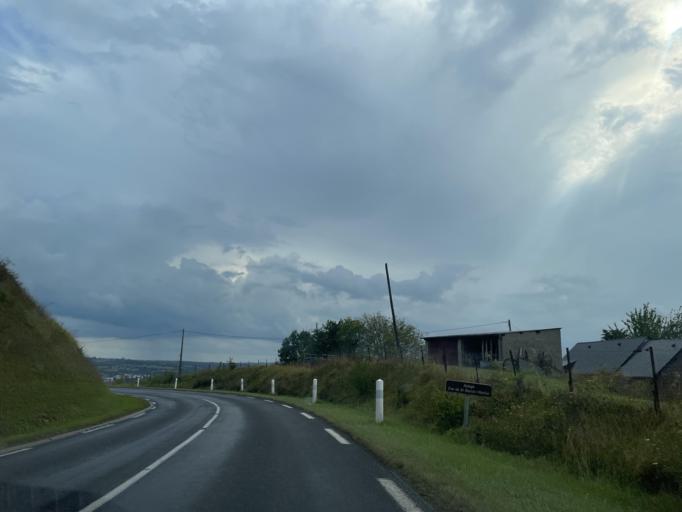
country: FR
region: Haute-Normandie
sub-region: Departement de la Seine-Maritime
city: Neufchatel-en-Bray
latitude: 49.7513
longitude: 1.4232
